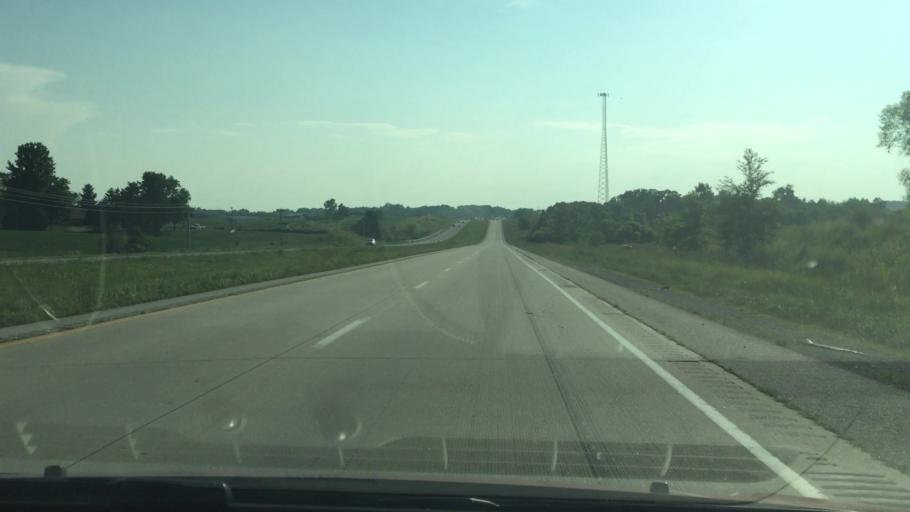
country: US
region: Iowa
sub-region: Cedar County
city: Durant
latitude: 41.5102
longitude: -90.9202
